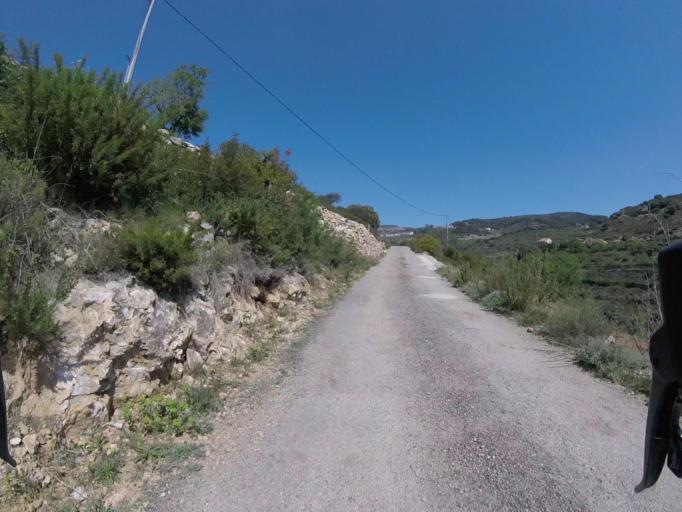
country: ES
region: Valencia
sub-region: Provincia de Castello
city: Sierra-Engarceran
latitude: 40.2569
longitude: -0.0246
